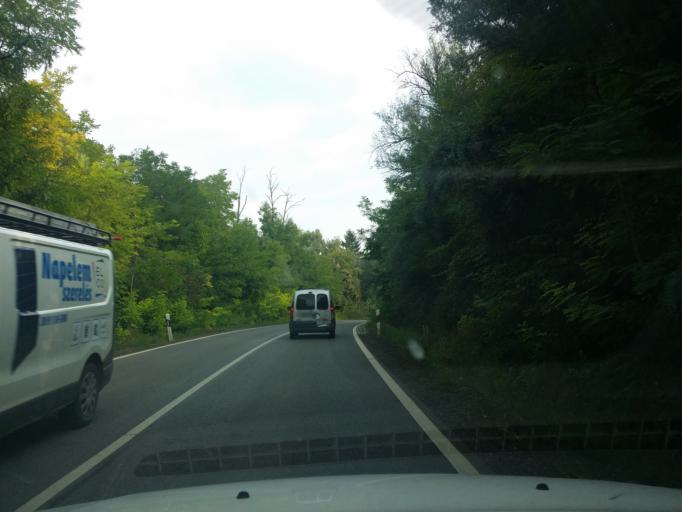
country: HU
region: Pest
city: Acsa
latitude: 47.7952
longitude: 19.3781
